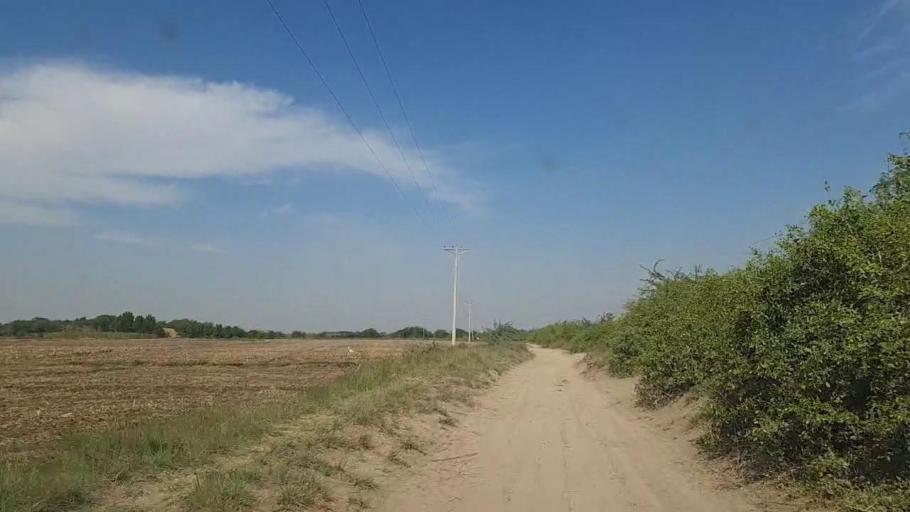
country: PK
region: Sindh
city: Bulri
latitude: 24.8276
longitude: 68.2707
